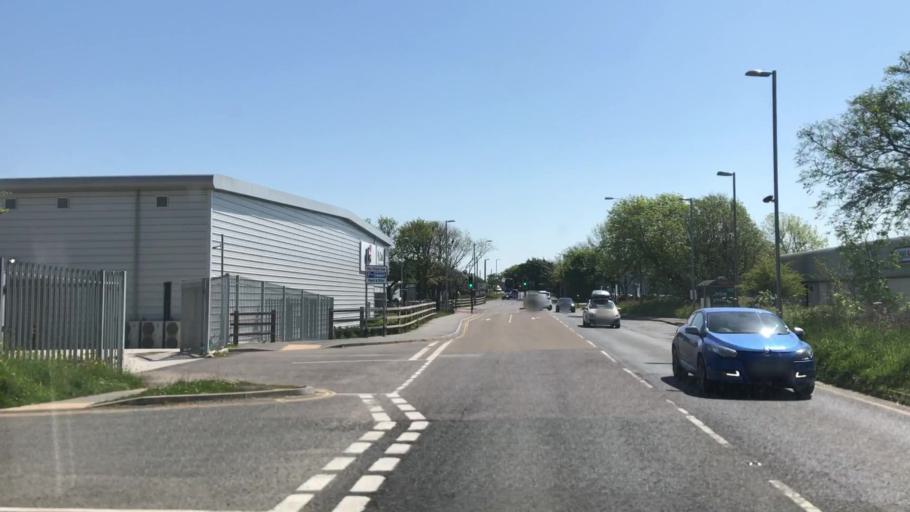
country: GB
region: England
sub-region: Cornwall
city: Chacewater
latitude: 50.2637
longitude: -5.1219
